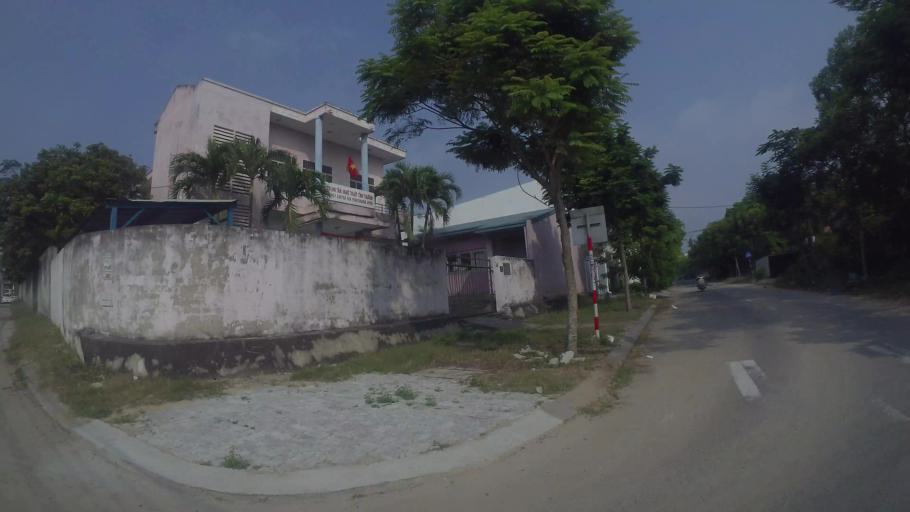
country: VN
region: Da Nang
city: Ngu Hanh Son
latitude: 16.0281
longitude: 108.2462
